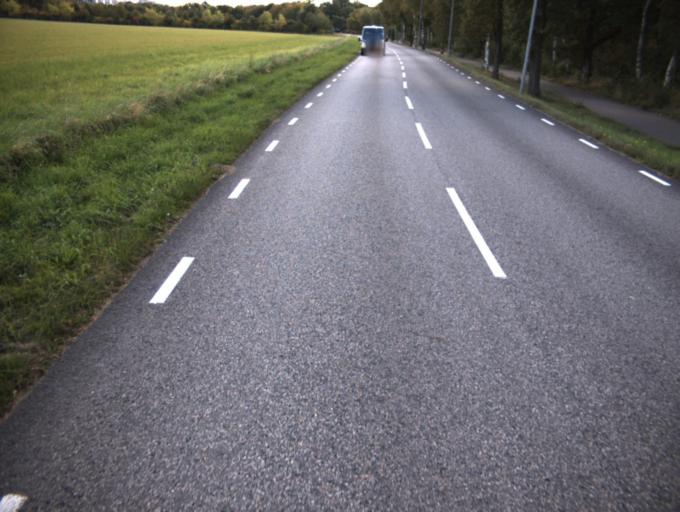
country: SE
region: Skane
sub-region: Helsingborg
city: Helsingborg
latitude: 56.0759
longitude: 12.6925
